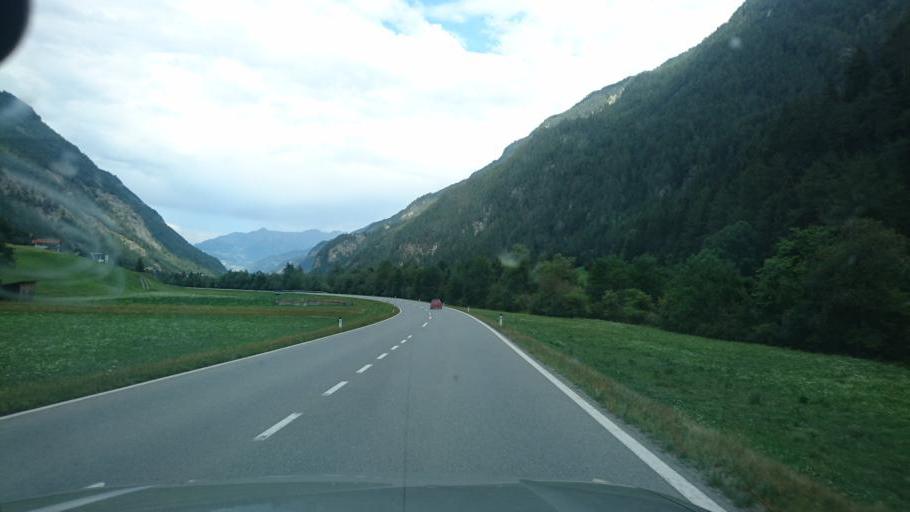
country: AT
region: Tyrol
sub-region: Politischer Bezirk Landeck
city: Pfunds
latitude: 46.9778
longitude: 10.5564
